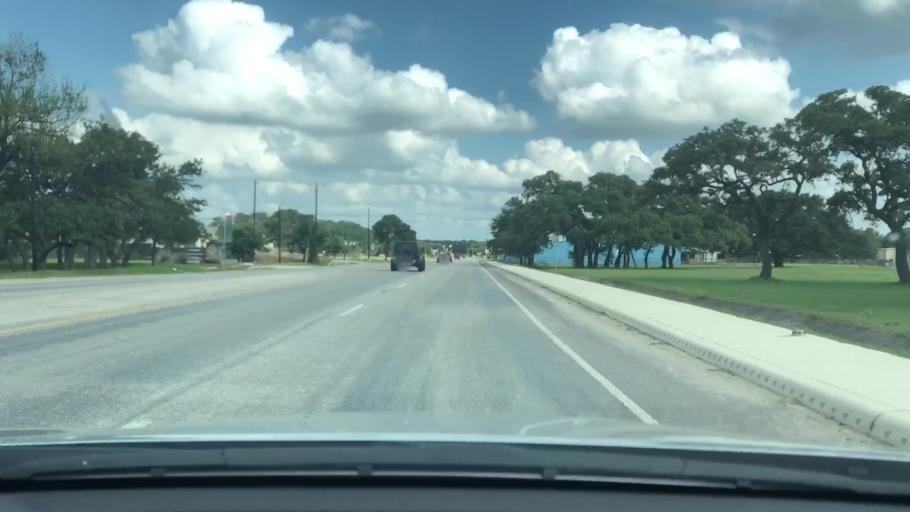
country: US
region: Texas
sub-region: Kendall County
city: Boerne
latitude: 29.7892
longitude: -98.7115
